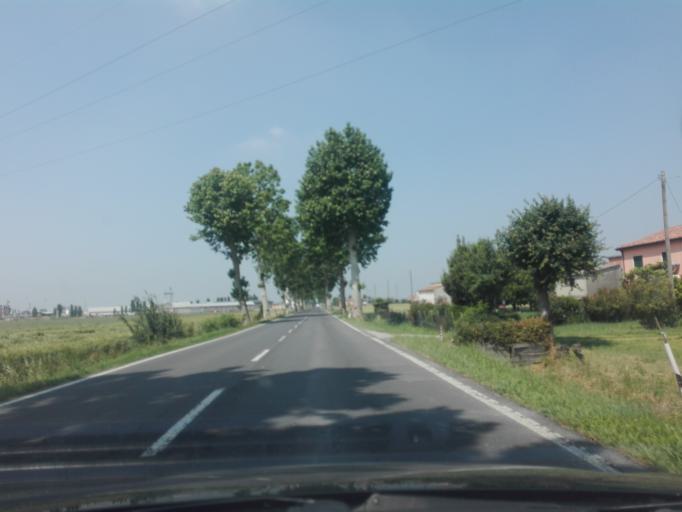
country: IT
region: Veneto
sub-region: Provincia di Rovigo
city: Lama Pezzoli
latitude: 45.0634
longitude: 11.9347
